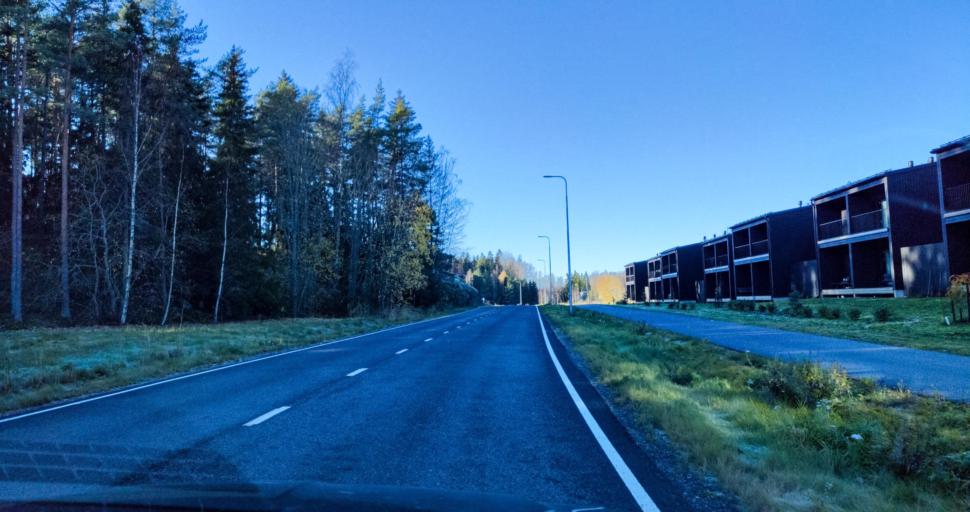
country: FI
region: Varsinais-Suomi
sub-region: Turku
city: Turku
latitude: 60.4054
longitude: 22.2141
